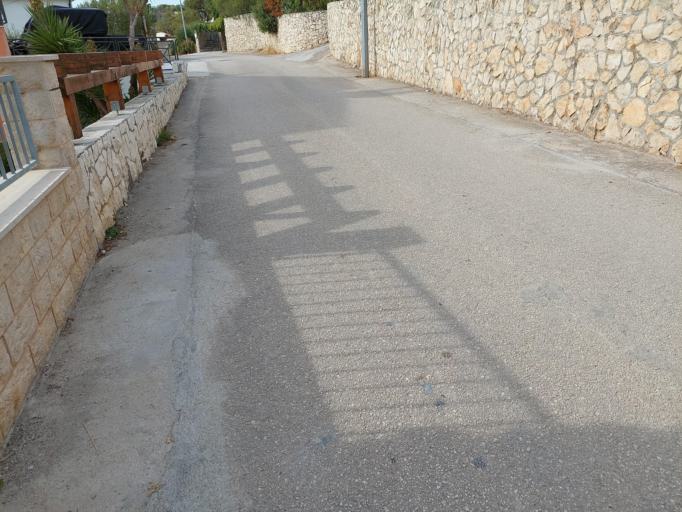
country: HR
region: Splitsko-Dalmatinska
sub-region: Grad Trogir
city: Trogir
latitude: 43.4921
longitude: 16.2767
